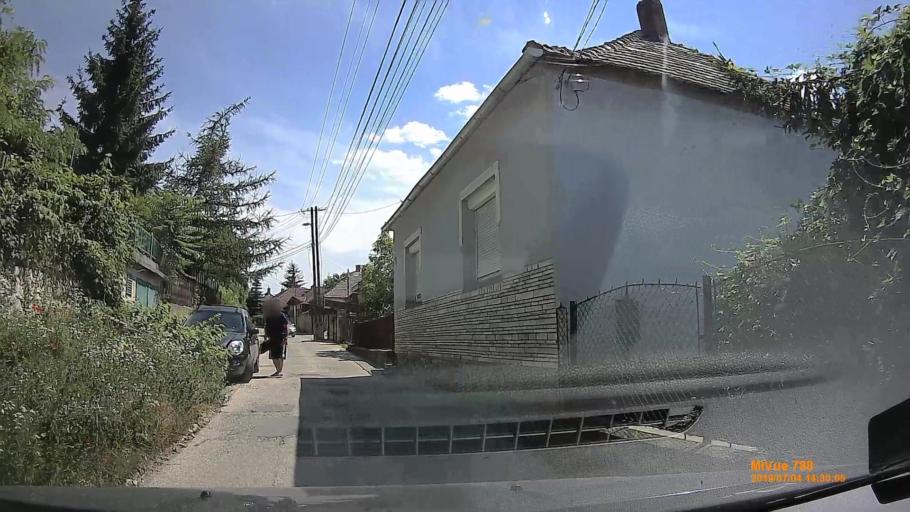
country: HU
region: Fejer
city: Szarliget
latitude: 47.5480
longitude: 18.4505
